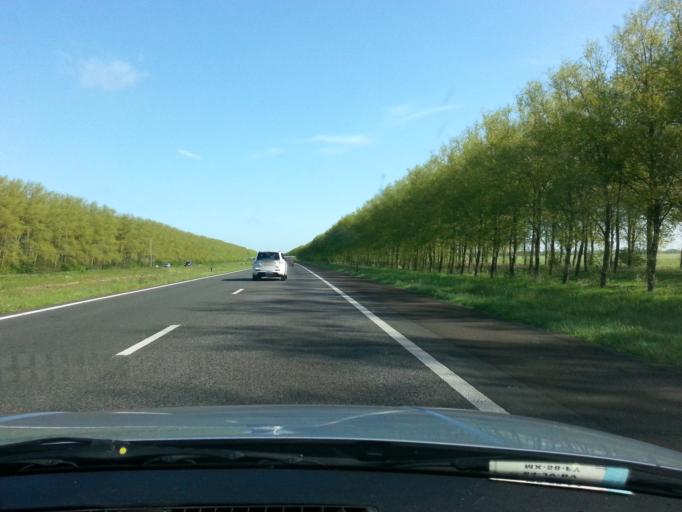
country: NL
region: Flevoland
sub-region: Gemeente Lelystad
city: Lelystad
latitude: 52.5114
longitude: 5.5337
